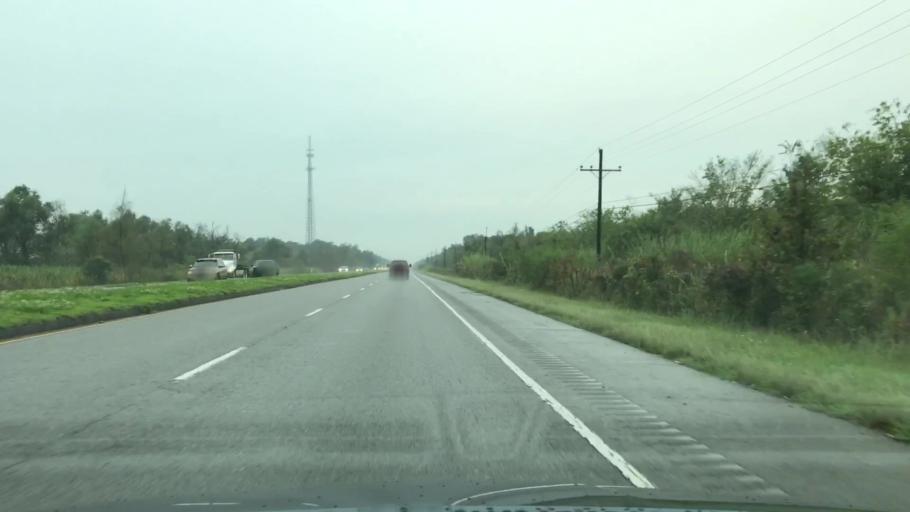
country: US
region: Louisiana
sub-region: Saint Charles Parish
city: Des Allemands
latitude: 29.7864
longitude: -90.5183
